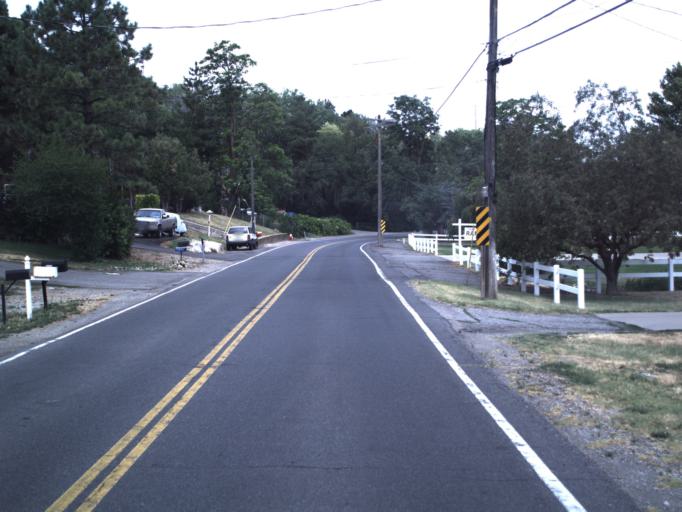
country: US
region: Utah
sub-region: Weber County
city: Riverdale
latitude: 41.1548
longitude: -111.9975
